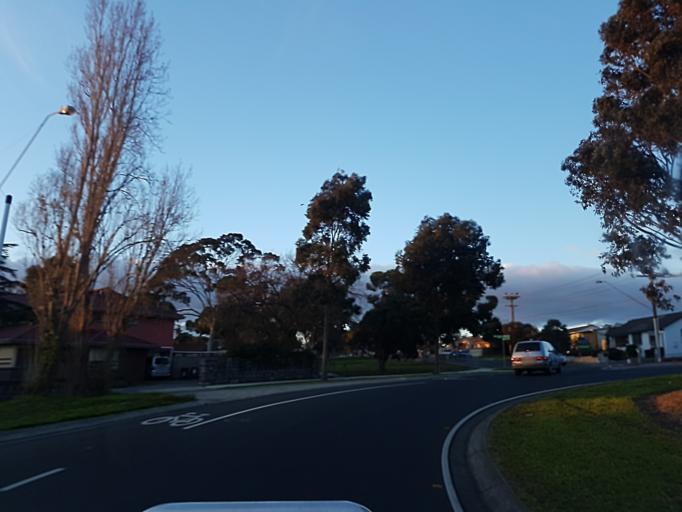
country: AU
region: Victoria
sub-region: Hume
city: Broadmeadows
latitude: -37.6758
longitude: 144.9288
